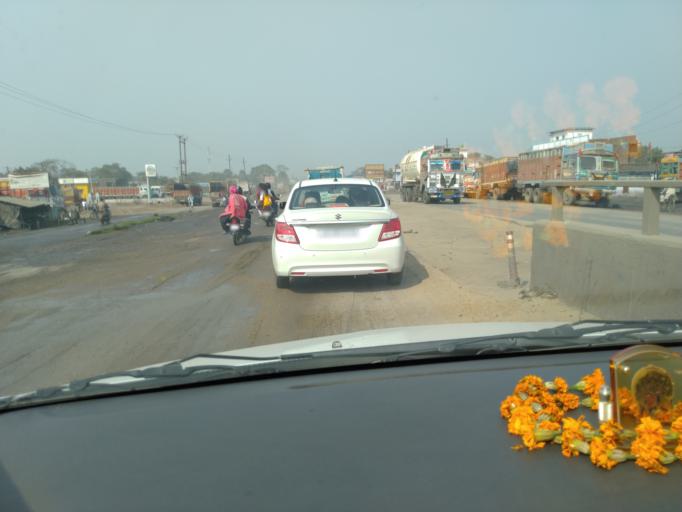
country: IN
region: Bihar
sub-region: Rohtas
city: Dehri
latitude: 24.9135
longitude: 84.1625
